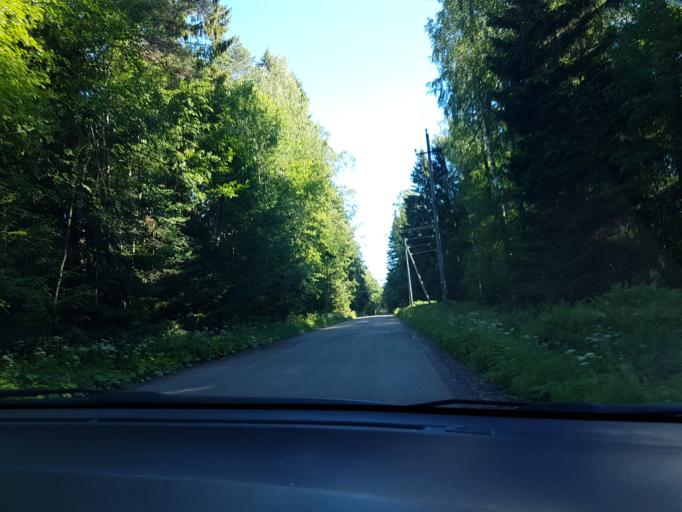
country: FI
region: Uusimaa
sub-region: Helsinki
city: Sibbo
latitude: 60.2649
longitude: 25.2275
